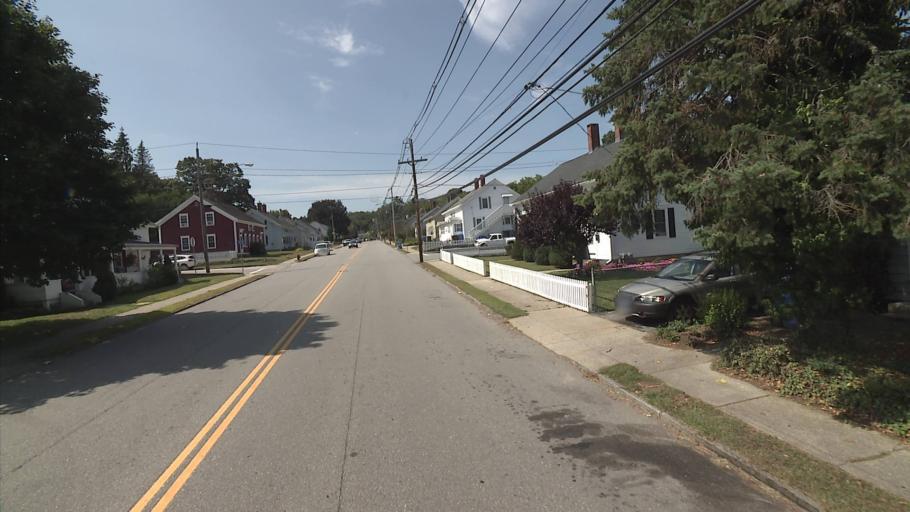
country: US
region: Connecticut
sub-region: New London County
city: Lisbon
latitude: 41.5697
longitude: -72.0498
